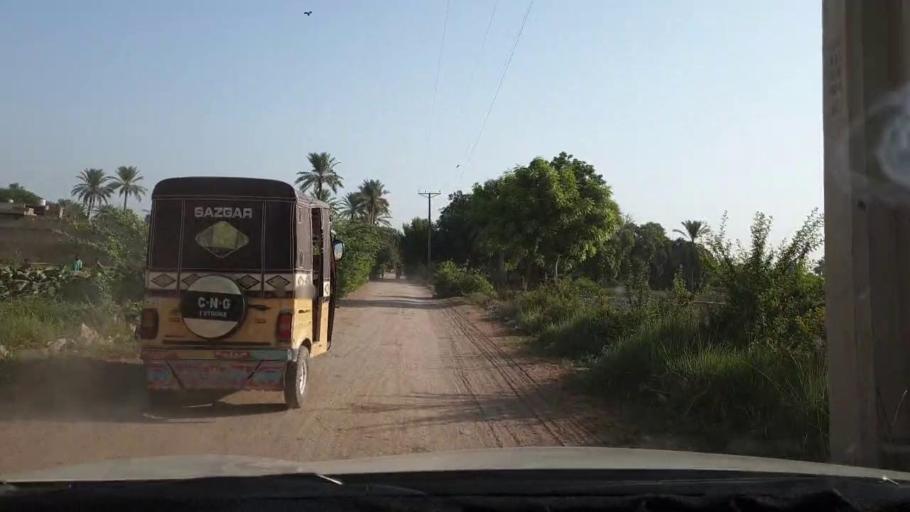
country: PK
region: Sindh
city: Larkana
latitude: 27.5497
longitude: 68.2315
